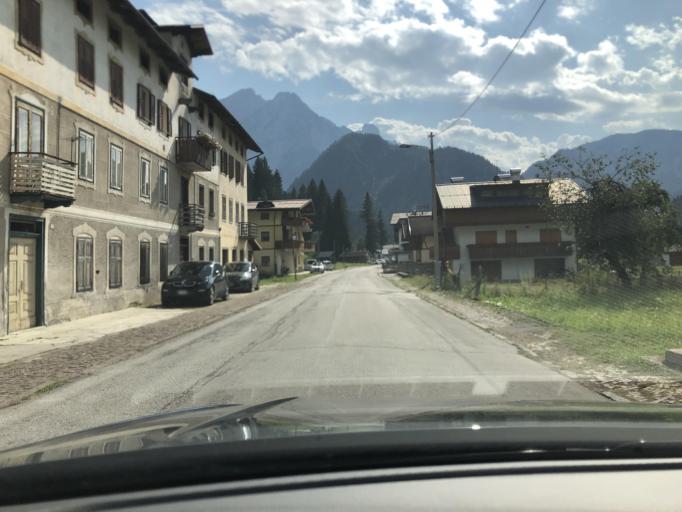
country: IT
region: Veneto
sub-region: Provincia di Belluno
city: Santo Stefano di Cadore
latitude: 46.5573
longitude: 12.5552
